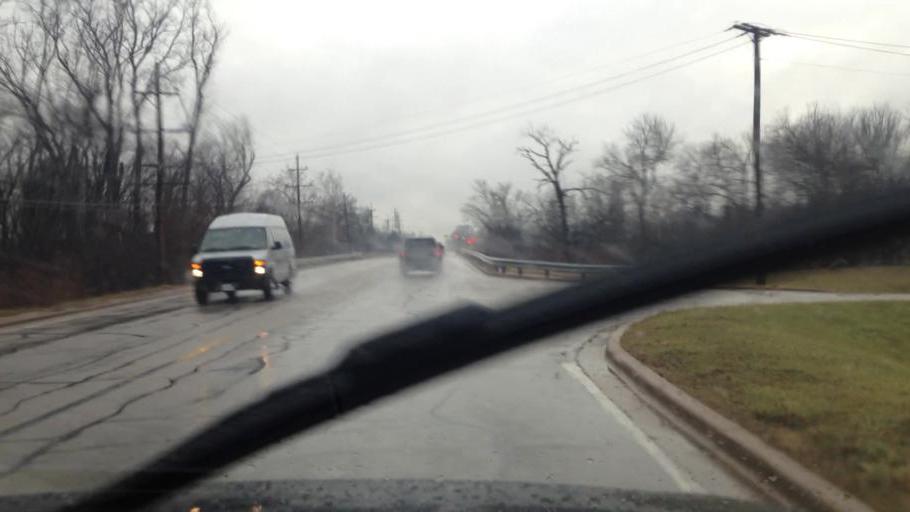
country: US
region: Illinois
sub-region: Will County
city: Ingalls Park
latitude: 41.5275
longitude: -88.0050
